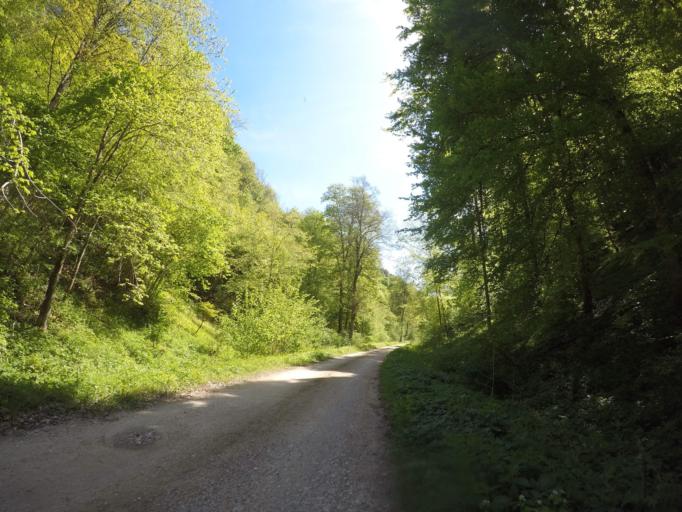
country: DE
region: Baden-Wuerttemberg
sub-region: Tuebingen Region
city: Schelklingen
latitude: 48.4029
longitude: 9.7364
